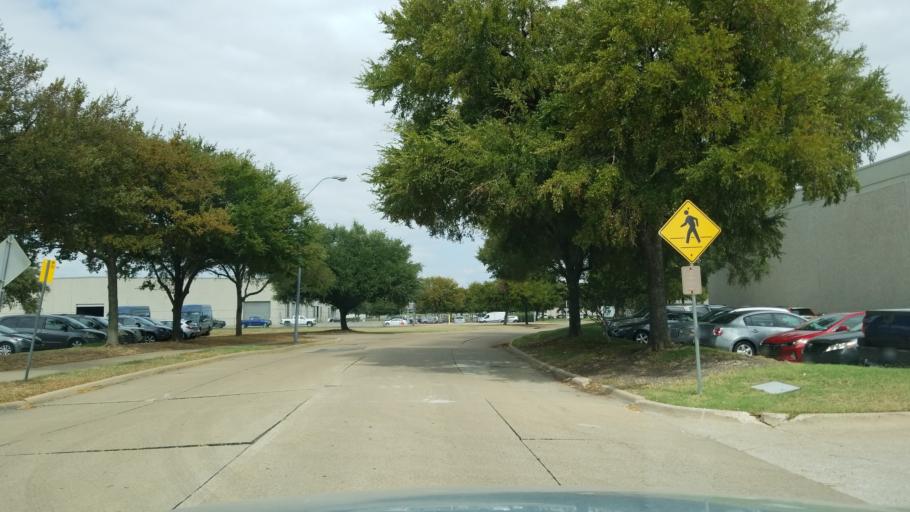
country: US
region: Texas
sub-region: Dallas County
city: Garland
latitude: 32.8907
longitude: -96.6788
